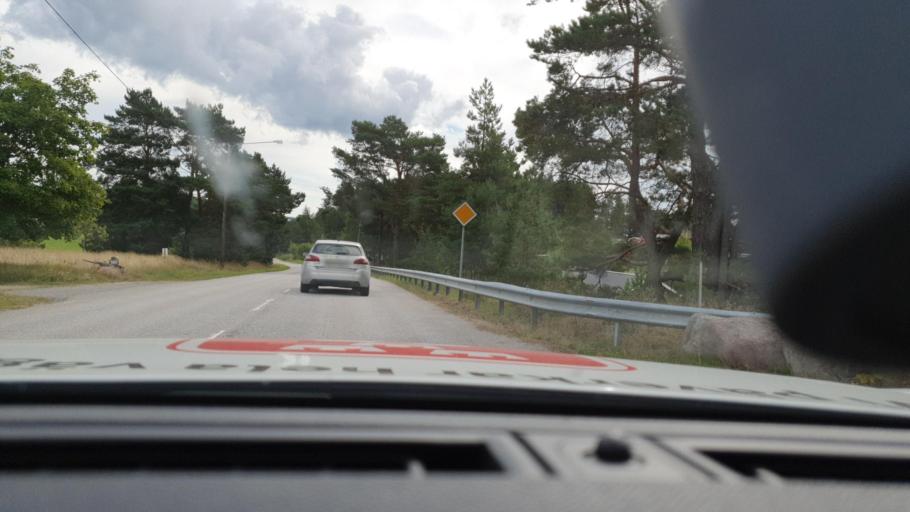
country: SE
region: Stockholm
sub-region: Norrtalje Kommun
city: Rimbo
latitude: 59.7275
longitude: 18.4919
